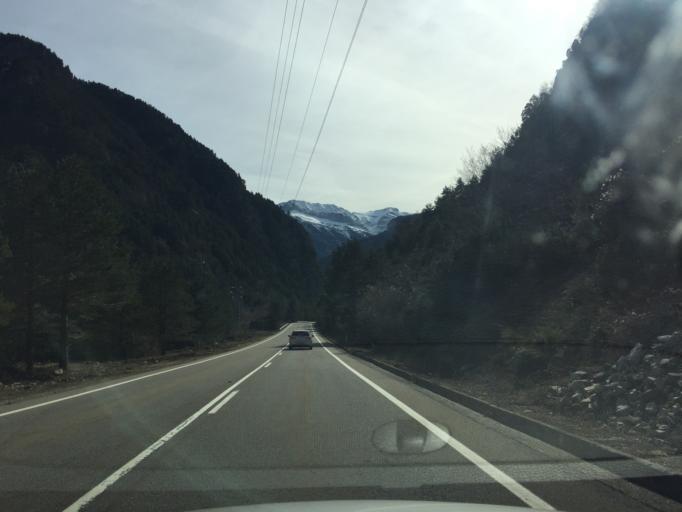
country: ES
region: Aragon
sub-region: Provincia de Huesca
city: Bielsa
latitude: 42.6727
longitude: 0.2147
